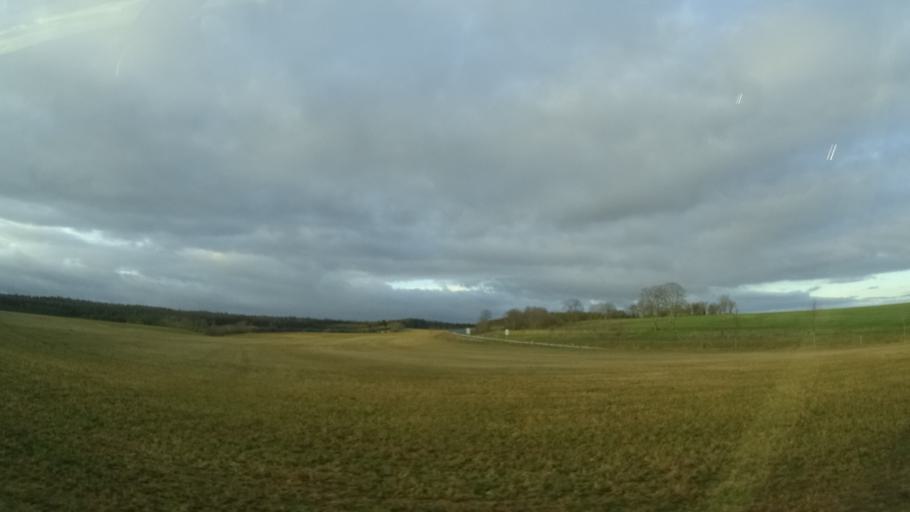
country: DE
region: Thuringia
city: Bad Blankenburg
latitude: 50.7297
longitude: 11.2385
